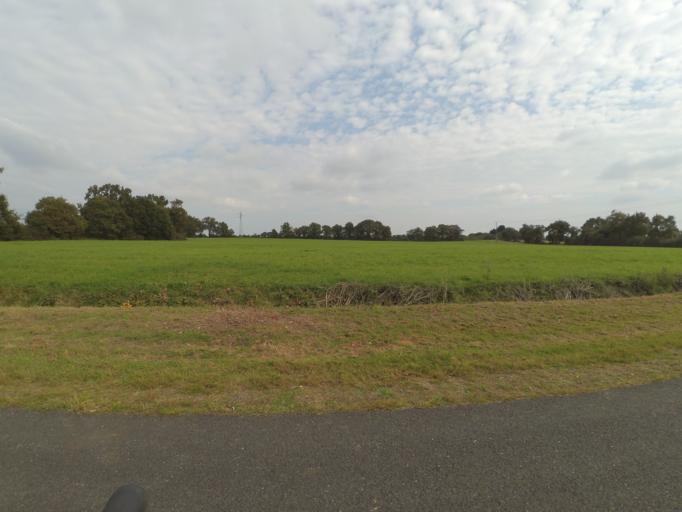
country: FR
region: Pays de la Loire
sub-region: Departement de la Vendee
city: Bouffere
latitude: 46.9755
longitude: -1.3500
